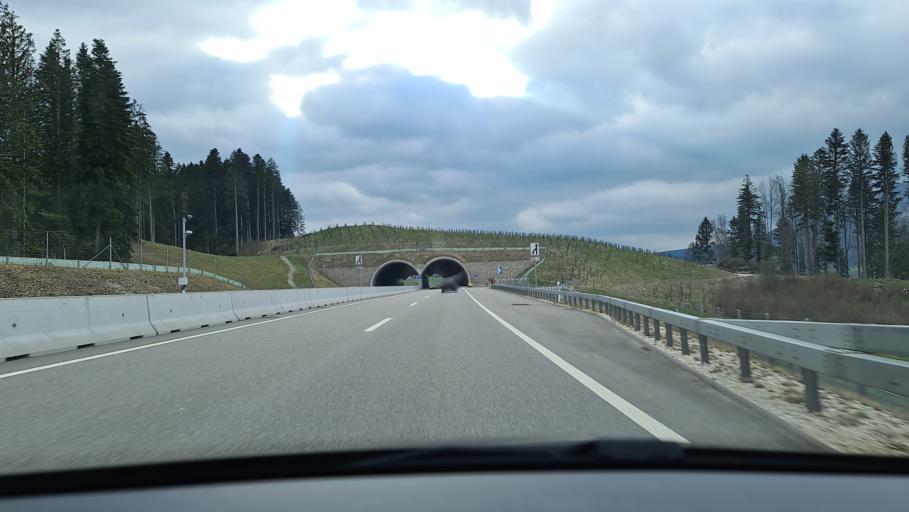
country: CH
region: Bern
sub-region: Jura bernois
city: Bevilard
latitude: 47.2305
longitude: 7.2807
